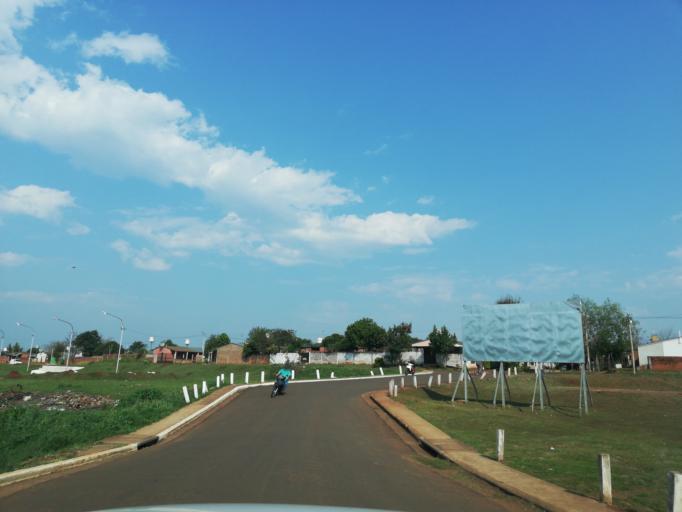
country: AR
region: Misiones
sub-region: Departamento de Capital
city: Posadas
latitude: -27.4319
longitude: -55.8755
